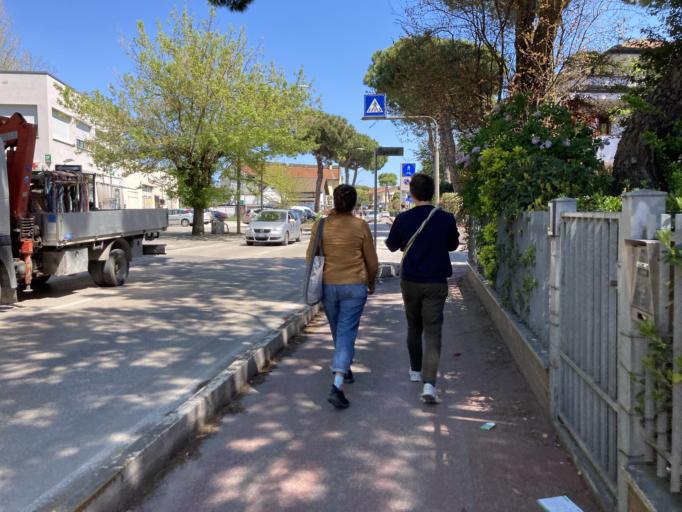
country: IT
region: Emilia-Romagna
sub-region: Provincia di Ravenna
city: Cervia
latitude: 44.2597
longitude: 12.3417
